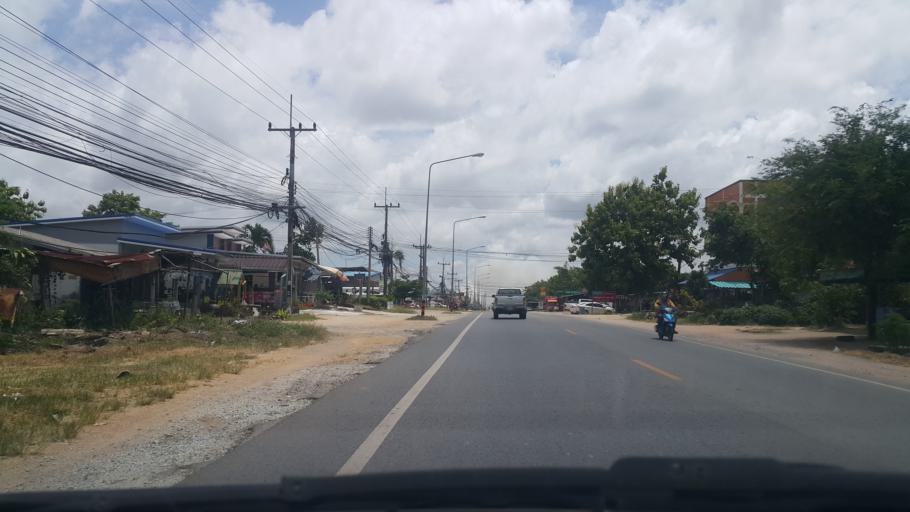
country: TH
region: Rayong
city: Ban Chang
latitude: 12.7437
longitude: 101.0419
